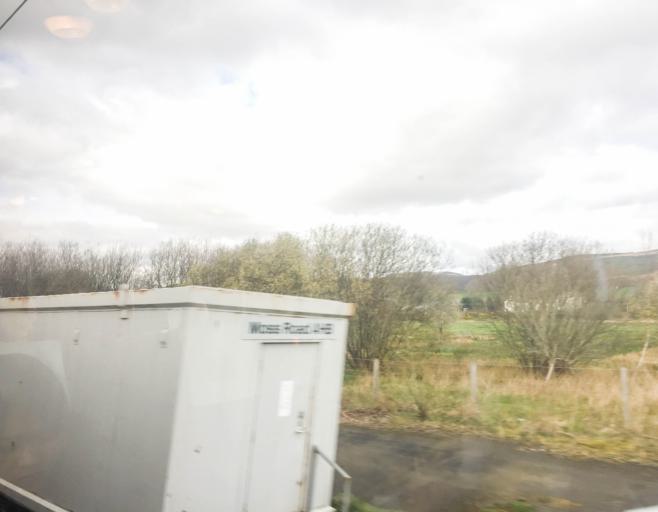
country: GB
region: Scotland
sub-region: Argyll and Bute
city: Helensburgh
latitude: 55.9822
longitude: -4.6905
